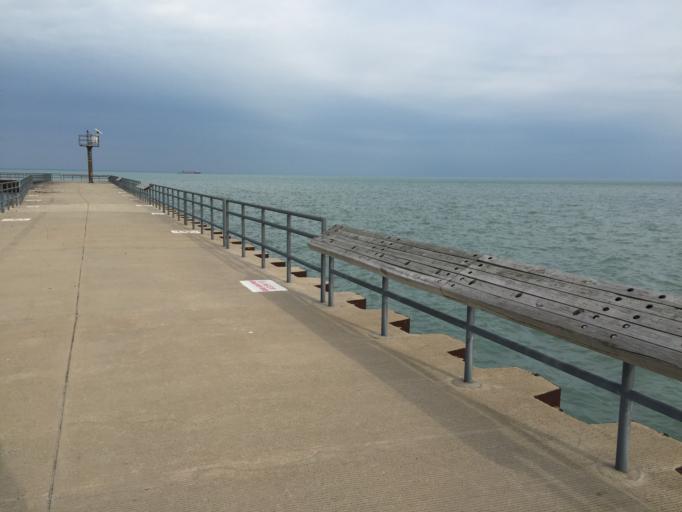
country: US
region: Illinois
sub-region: Cook County
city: Chicago
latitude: 41.7813
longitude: -87.5696
